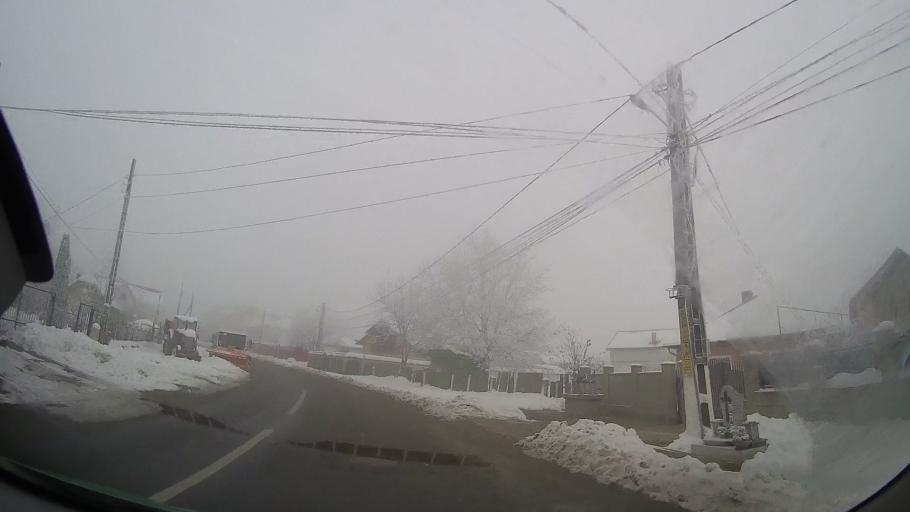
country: RO
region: Neamt
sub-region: Comuna Sabaoani
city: Sabaoani
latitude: 47.0167
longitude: 26.8660
